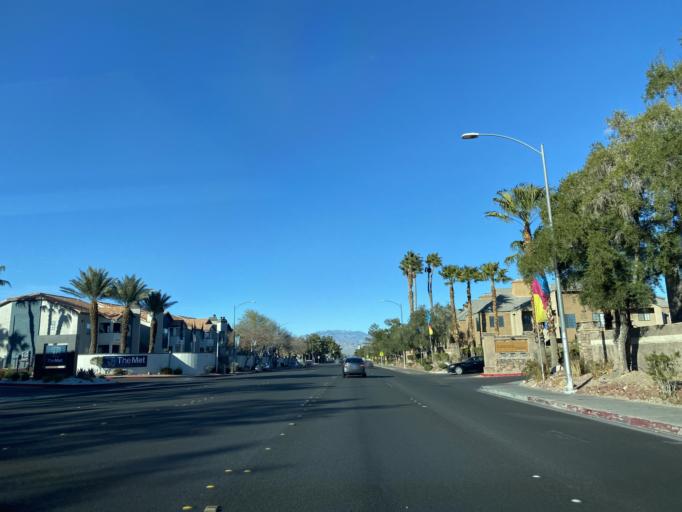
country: US
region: Nevada
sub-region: Clark County
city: Spring Valley
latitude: 36.2086
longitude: -115.2422
